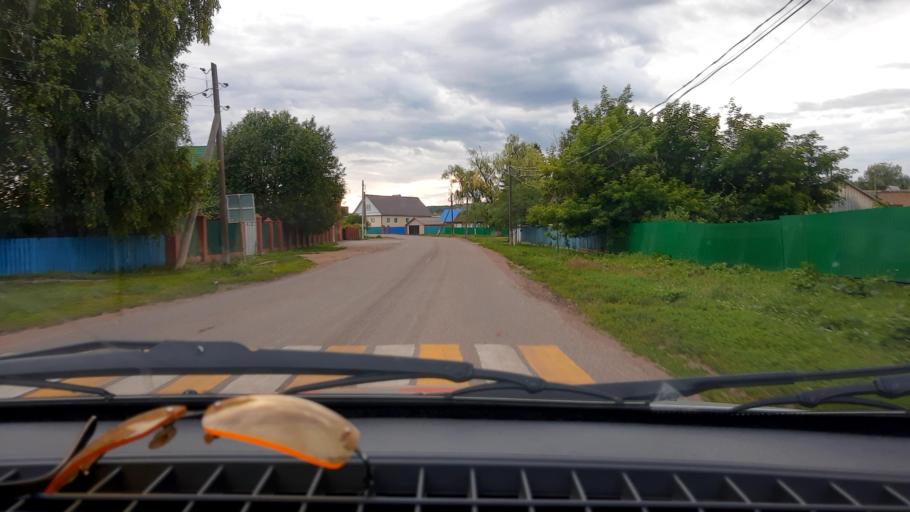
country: RU
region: Bashkortostan
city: Chishmy
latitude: 54.5600
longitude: 55.4680
